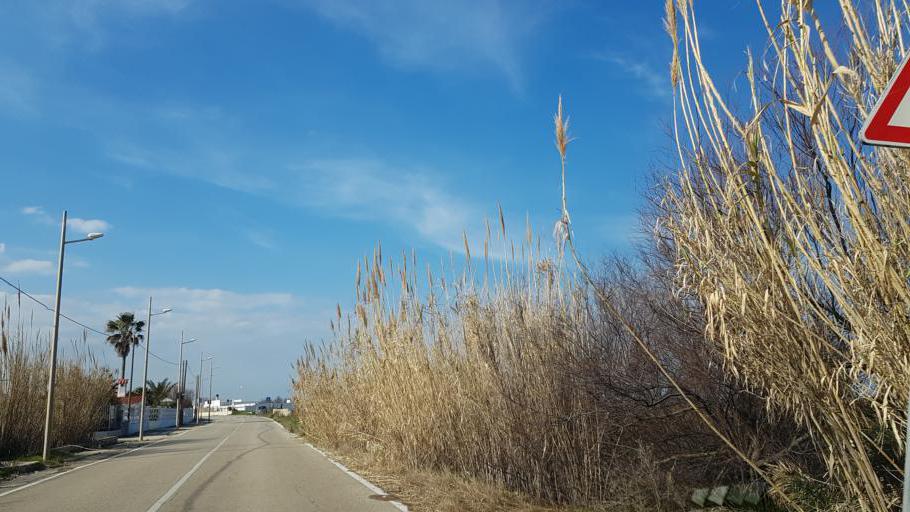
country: IT
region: Apulia
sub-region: Provincia di Brindisi
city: Brindisi
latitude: 40.6922
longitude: 17.8352
